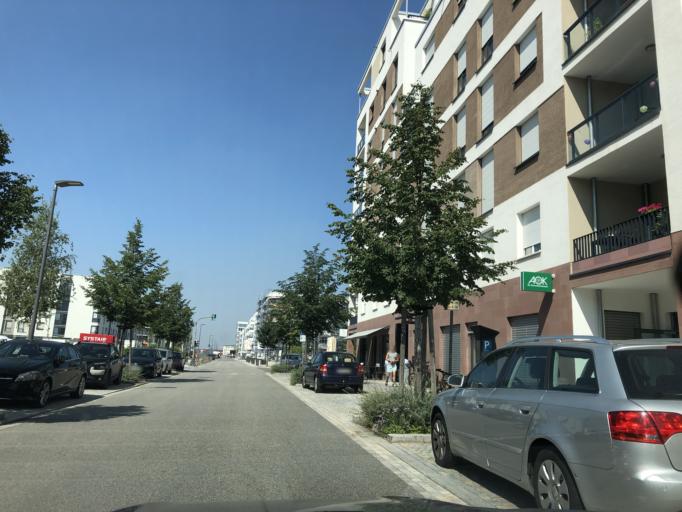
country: DE
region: Baden-Wuerttemberg
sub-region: Karlsruhe Region
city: Heidelberg
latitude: 49.4020
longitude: 8.6669
